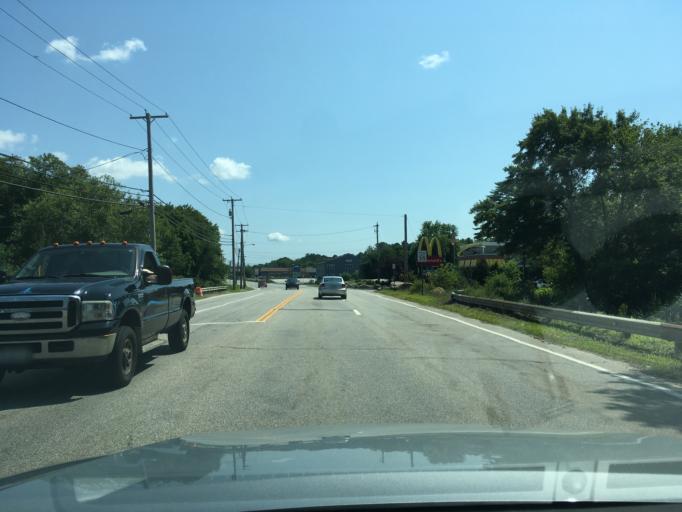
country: US
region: Rhode Island
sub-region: Kent County
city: West Warwick
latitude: 41.6790
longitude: -71.5813
